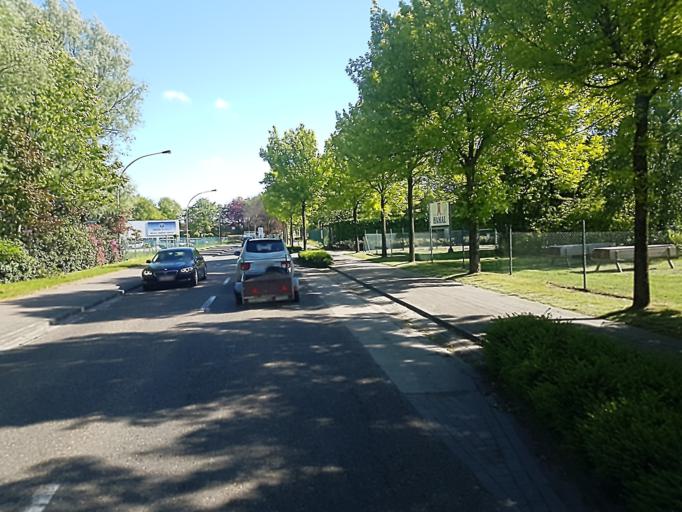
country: BE
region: Flanders
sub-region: Provincie Antwerpen
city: Turnhout
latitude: 51.3015
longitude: 4.9326
